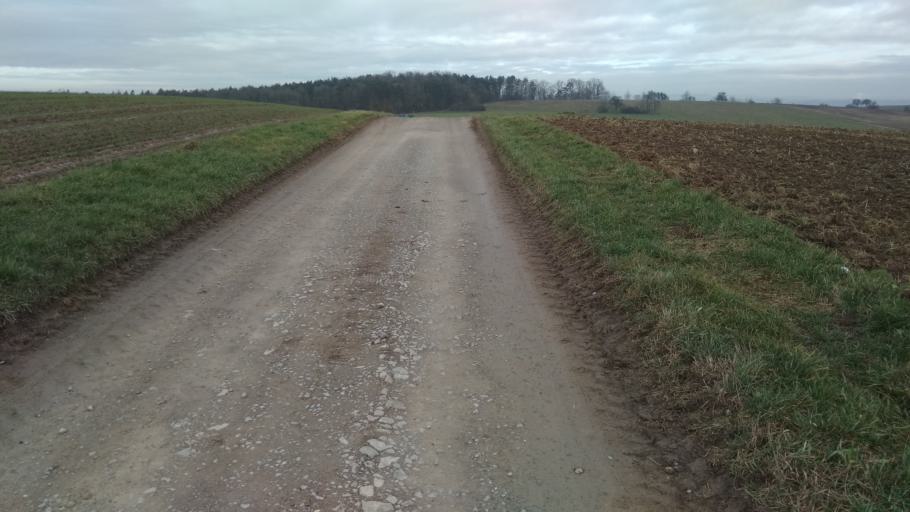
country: DE
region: Baden-Wuerttemberg
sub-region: Karlsruhe Region
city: Mosbach
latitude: 49.3580
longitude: 9.1755
